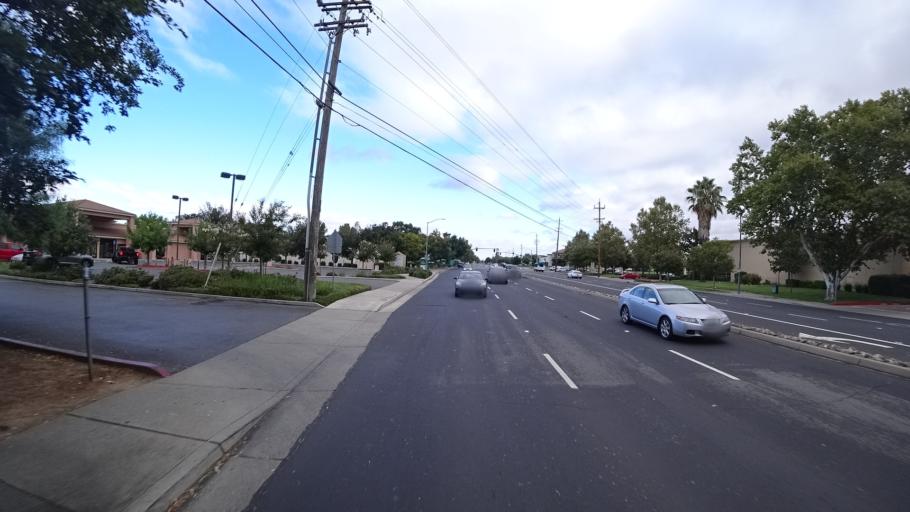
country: US
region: California
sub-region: Sacramento County
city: Laguna
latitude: 38.4222
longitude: -121.4180
